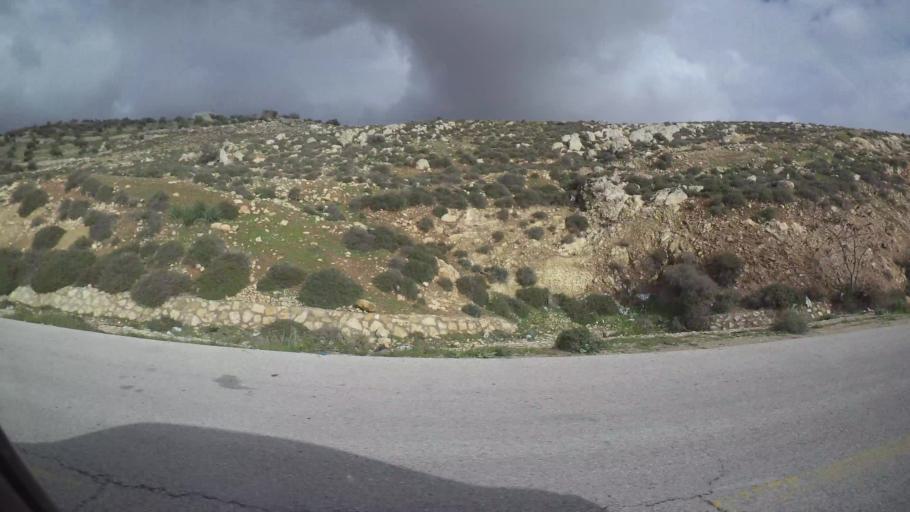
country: JO
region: Amman
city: Al Jubayhah
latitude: 32.0762
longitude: 35.8788
